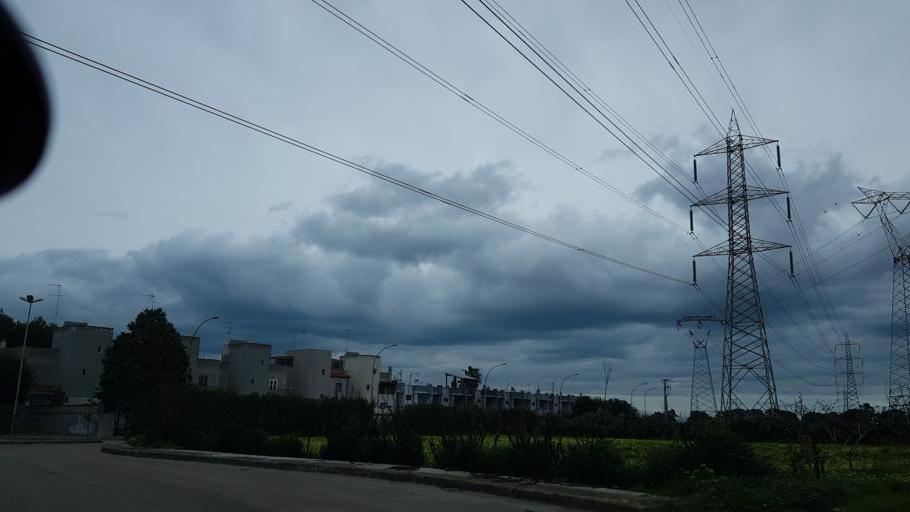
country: IT
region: Apulia
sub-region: Provincia di Brindisi
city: La Rosa
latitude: 40.6031
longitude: 17.9528
